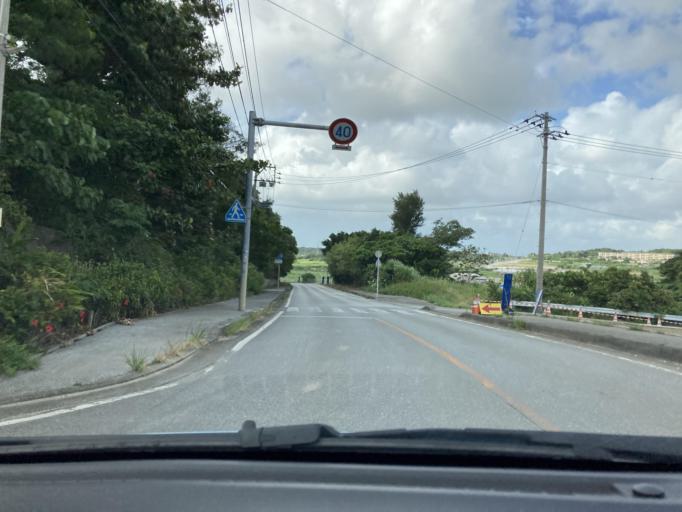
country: JP
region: Okinawa
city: Itoman
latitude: 26.1098
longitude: 127.6941
